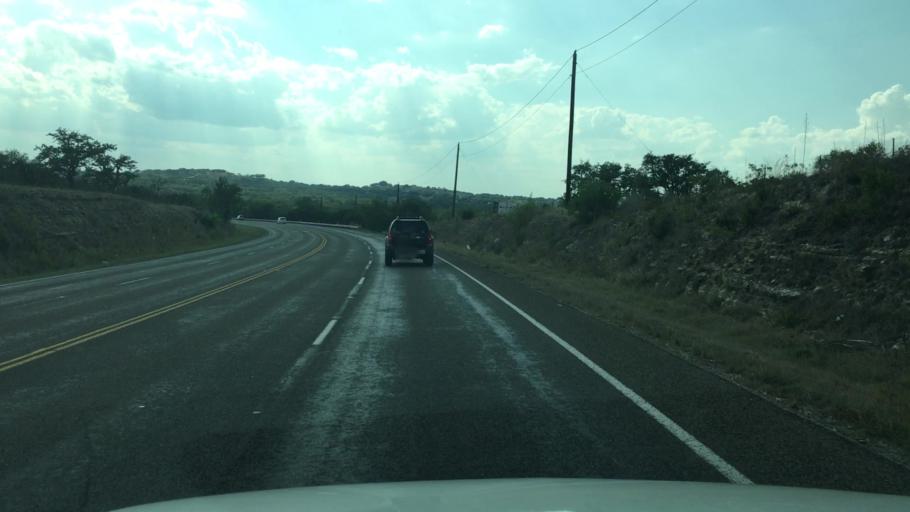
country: US
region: Texas
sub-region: Blanco County
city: Johnson City
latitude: 30.2106
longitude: -98.2778
